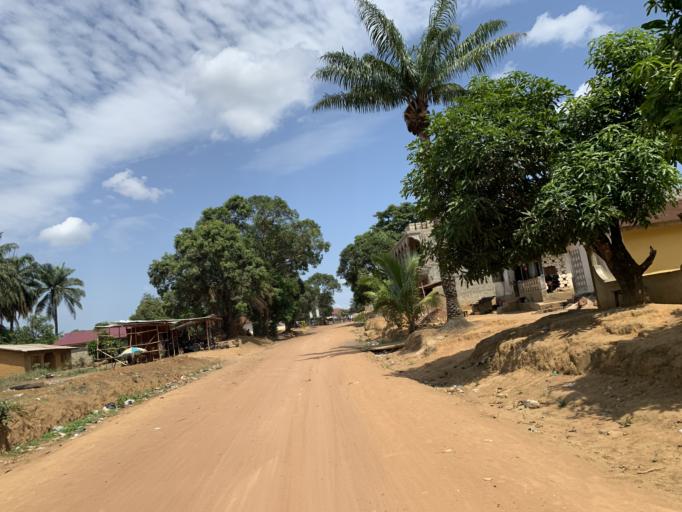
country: SL
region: Western Area
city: Waterloo
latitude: 8.3312
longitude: -13.0408
